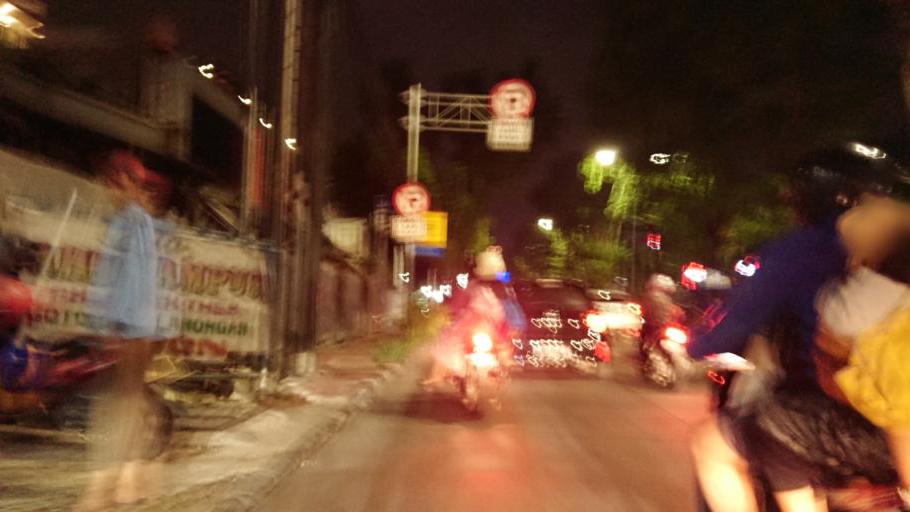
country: ID
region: Jakarta Raya
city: Jakarta
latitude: -6.2511
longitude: 106.7816
